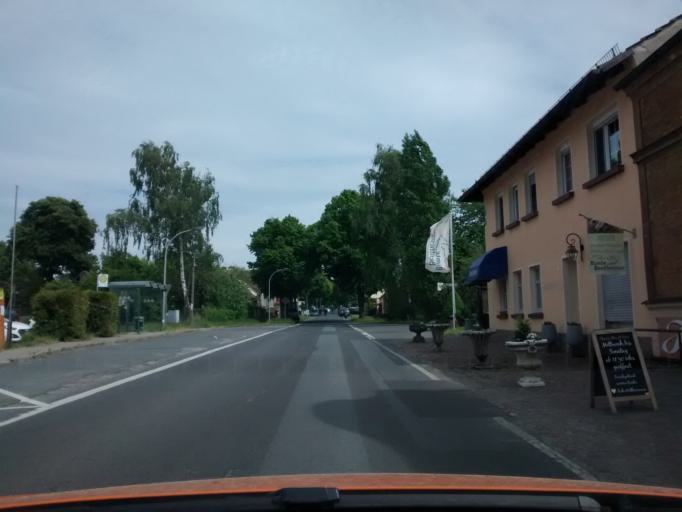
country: DE
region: Brandenburg
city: Ihlow
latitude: 51.8904
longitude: 13.3050
